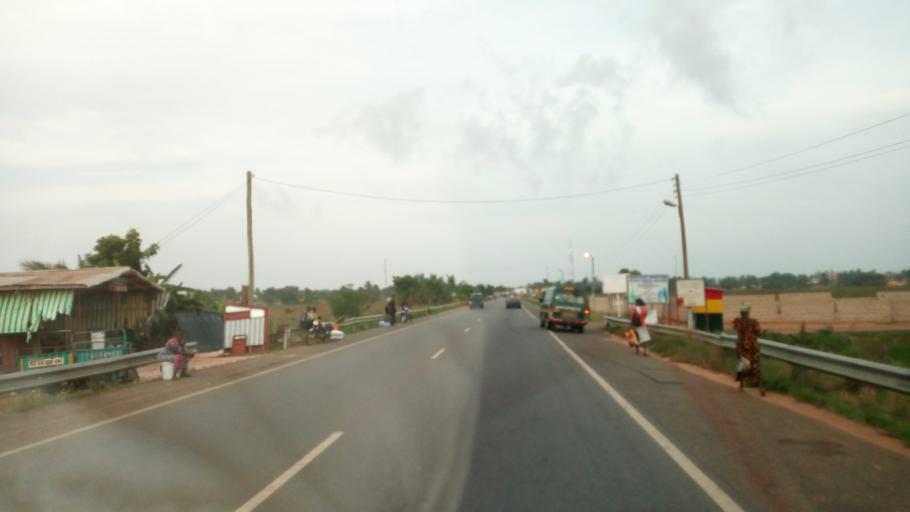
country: GH
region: Volta
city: Keta
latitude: 6.0771
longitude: 1.0426
